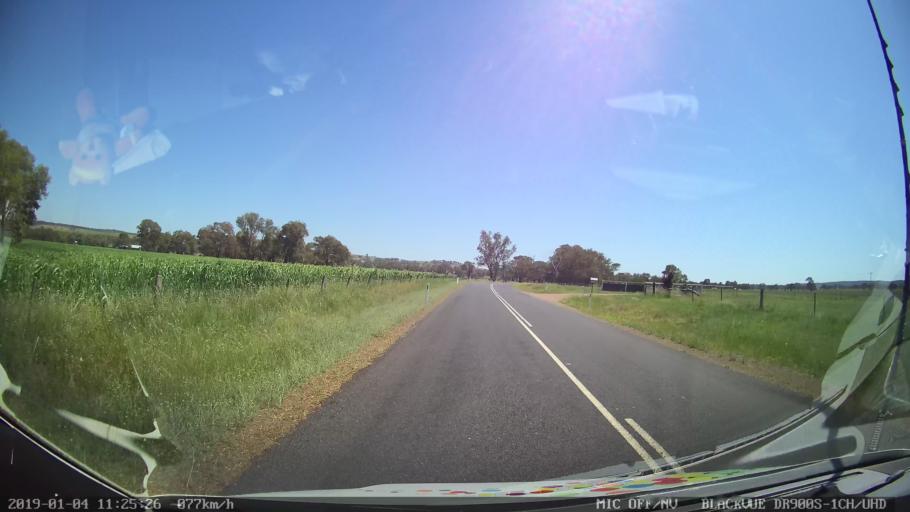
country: AU
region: New South Wales
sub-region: Cabonne
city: Molong
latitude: -33.1249
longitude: 148.7522
